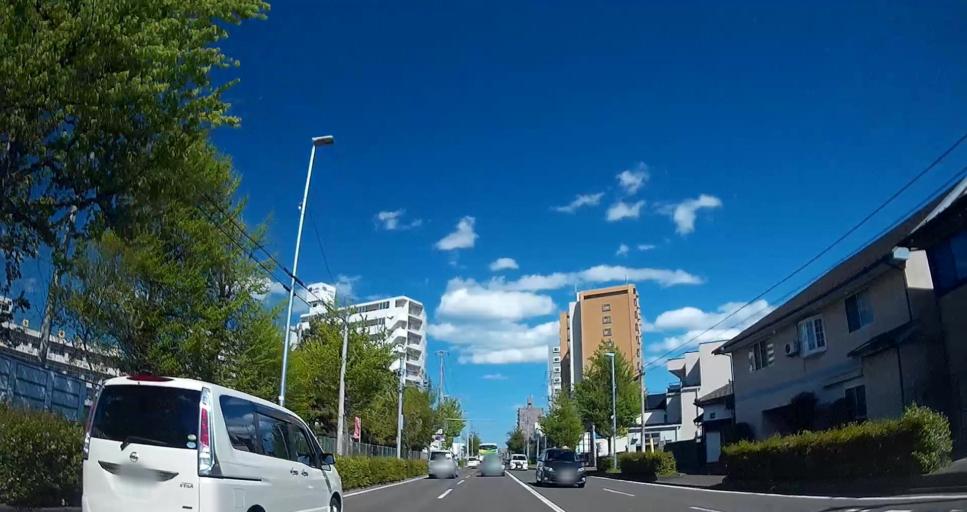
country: JP
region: Miyagi
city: Sendai-shi
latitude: 38.2537
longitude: 140.8991
